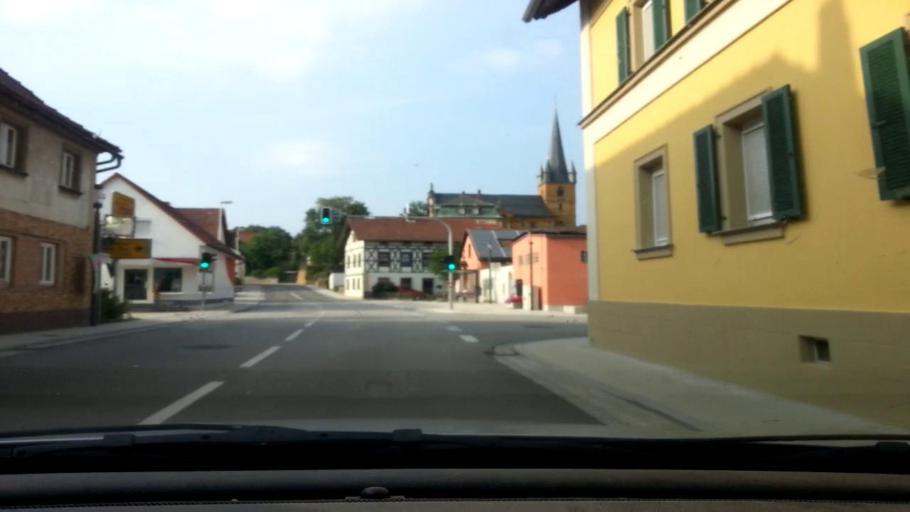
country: DE
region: Bavaria
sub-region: Upper Franconia
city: Litzendorf
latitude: 49.9111
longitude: 11.0101
